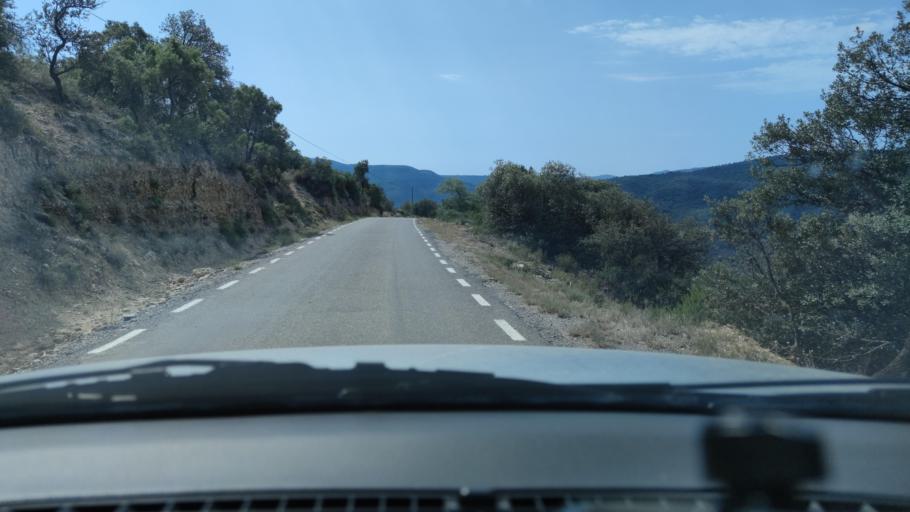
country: ES
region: Catalonia
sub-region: Provincia de Lleida
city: Ager
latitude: 42.0109
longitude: 0.8312
